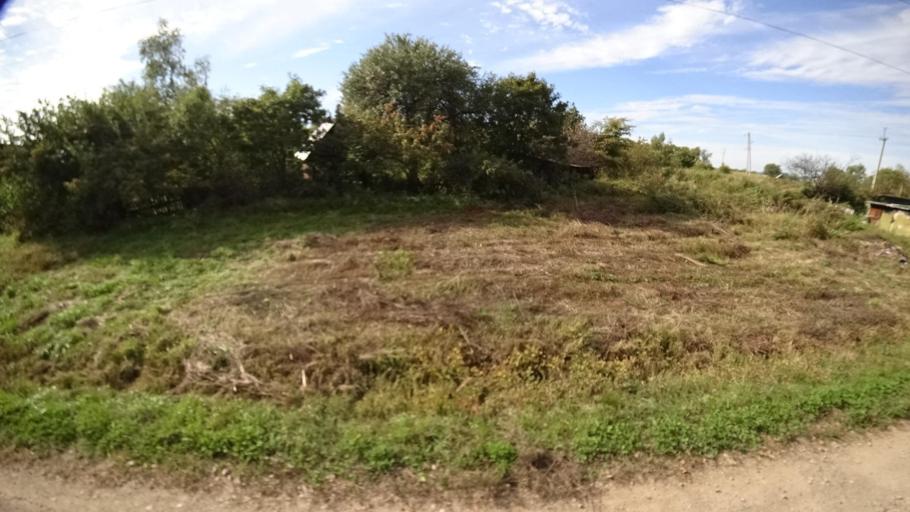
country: RU
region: Primorskiy
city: Dostoyevka
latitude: 44.2981
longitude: 133.4636
